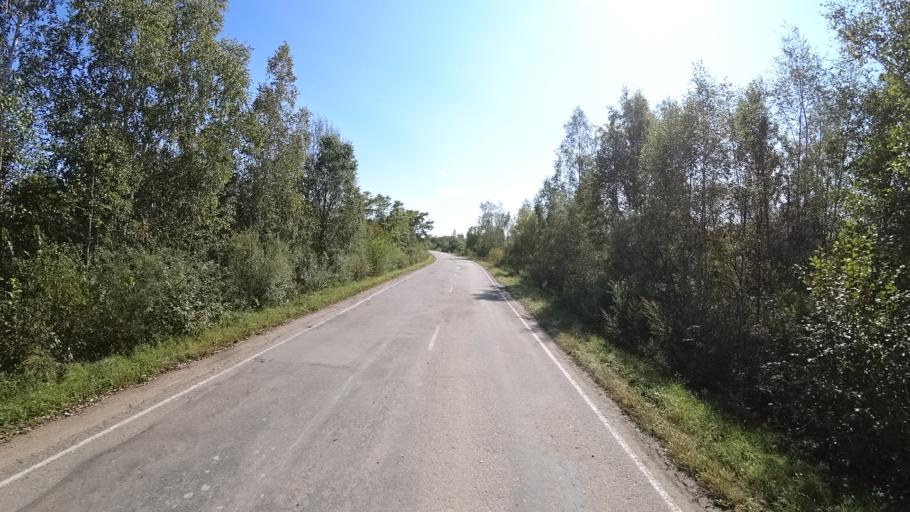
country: RU
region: Amur
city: Arkhara
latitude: 49.4032
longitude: 130.1287
